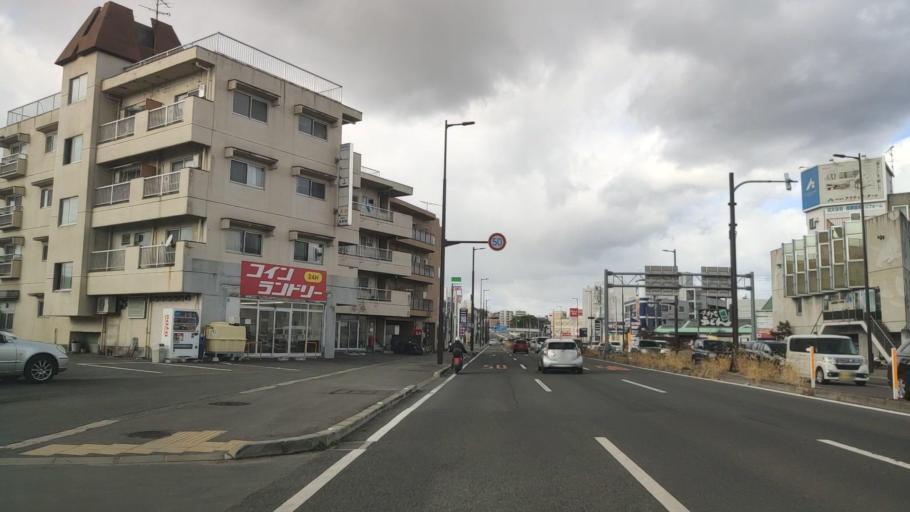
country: JP
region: Ehime
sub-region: Shikoku-chuo Shi
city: Matsuyama
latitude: 33.8307
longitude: 132.7800
